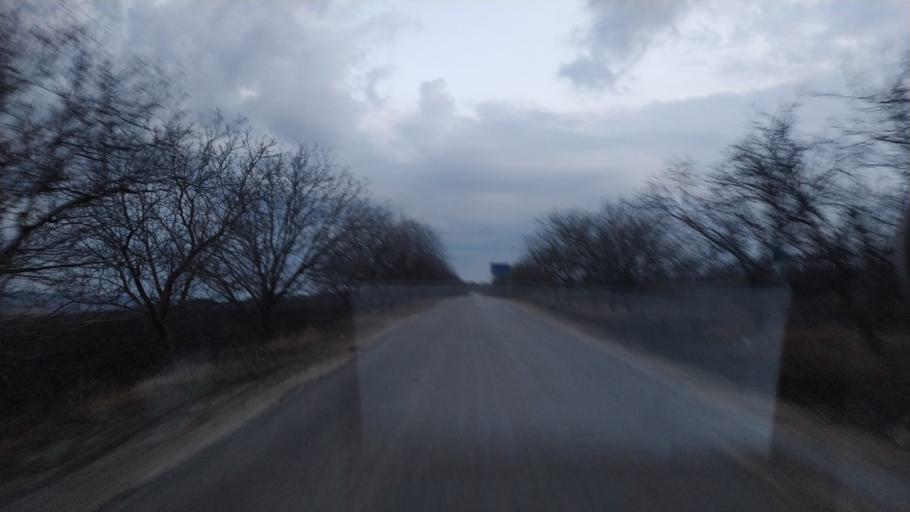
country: MD
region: Anenii Noi
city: Anenii Noi
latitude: 46.9354
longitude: 29.2858
